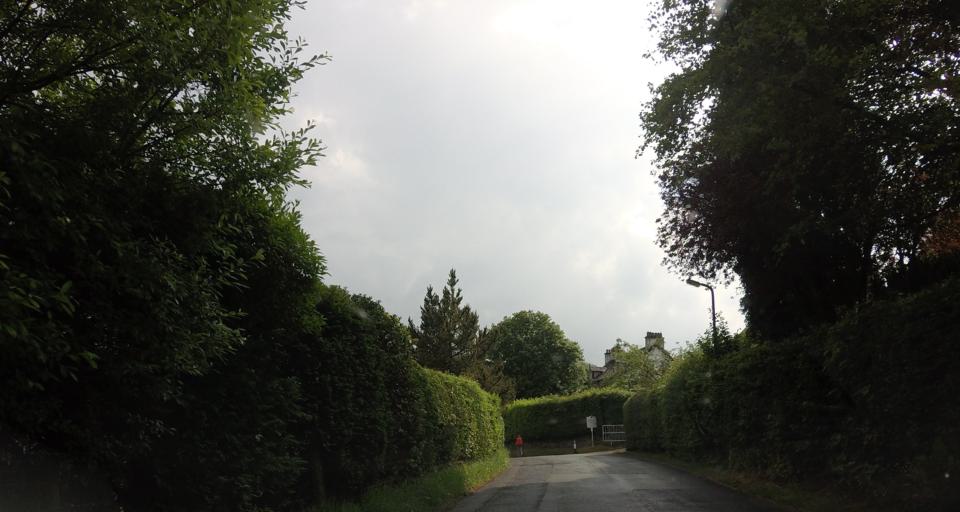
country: GB
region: England
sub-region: Cumbria
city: Keswick
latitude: 54.6042
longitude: -3.1889
